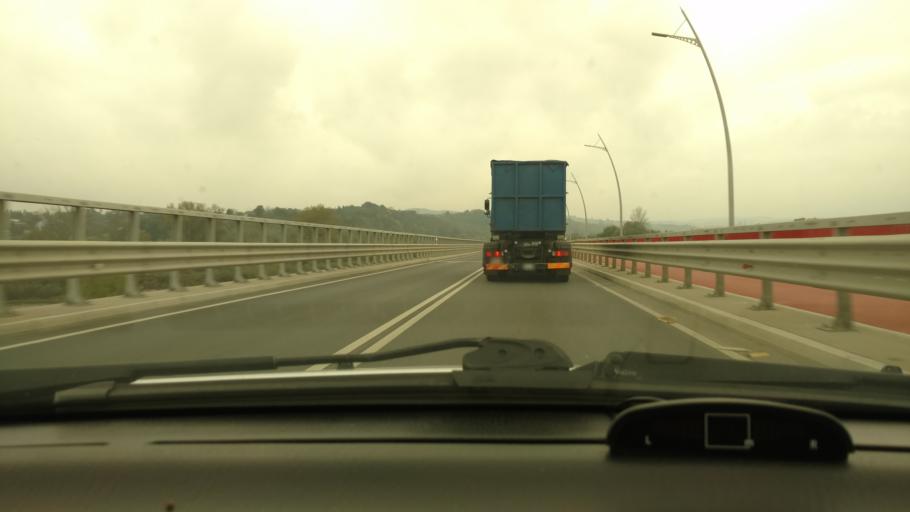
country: PL
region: Lesser Poland Voivodeship
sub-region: Powiat nowosadecki
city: Chelmiec
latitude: 49.6413
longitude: 20.6801
